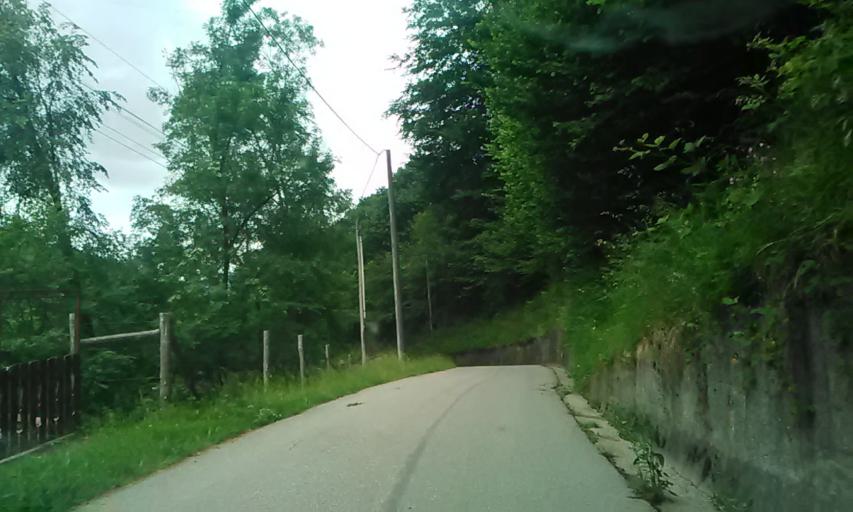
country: IT
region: Piedmont
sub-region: Provincia di Vercelli
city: Civiasco
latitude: 45.8151
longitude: 8.3098
